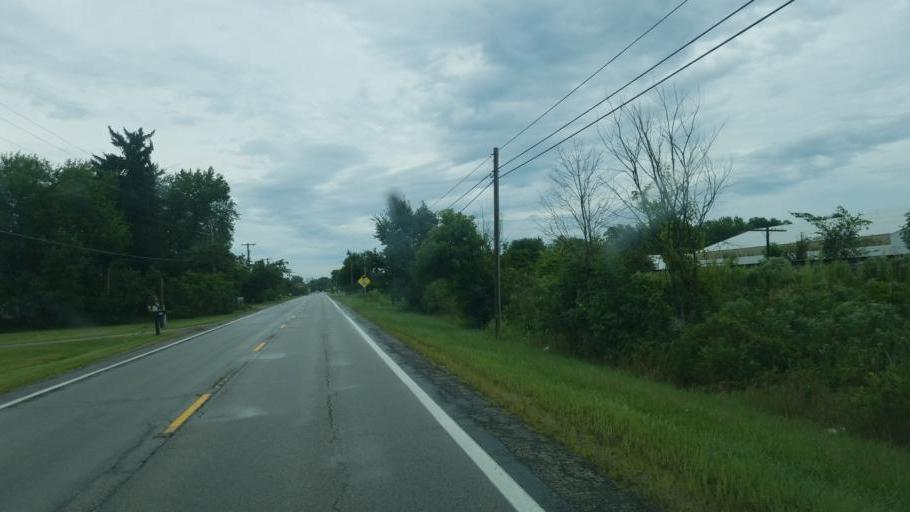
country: US
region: Ohio
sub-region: Delaware County
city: Ashley
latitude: 40.4036
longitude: -82.9591
